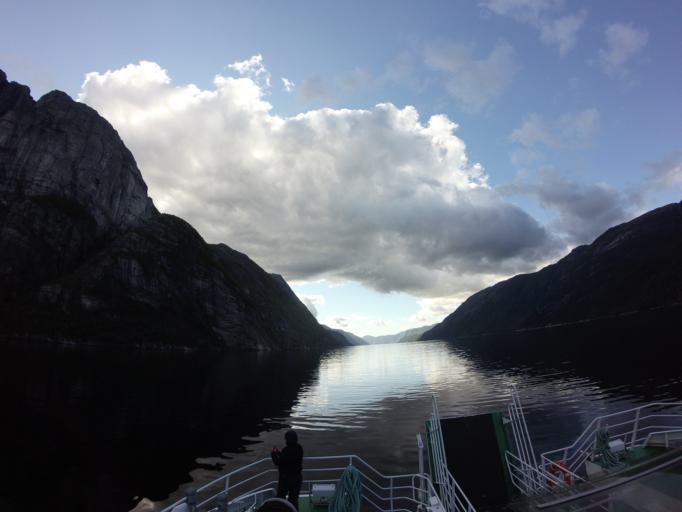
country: NO
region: Rogaland
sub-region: Hjelmeland
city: Hjelmelandsvagen
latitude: 59.0340
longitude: 6.5279
